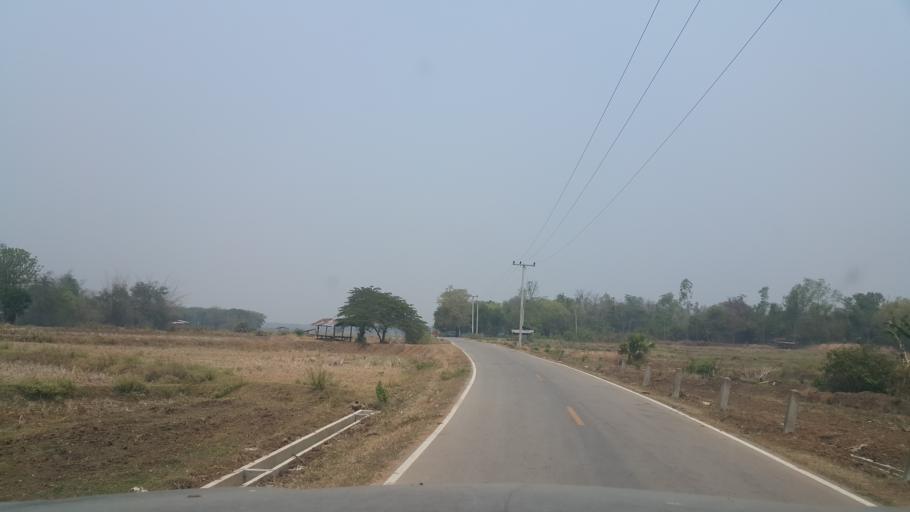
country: TH
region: Lampang
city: Sop Prap
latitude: 17.8933
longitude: 99.3150
